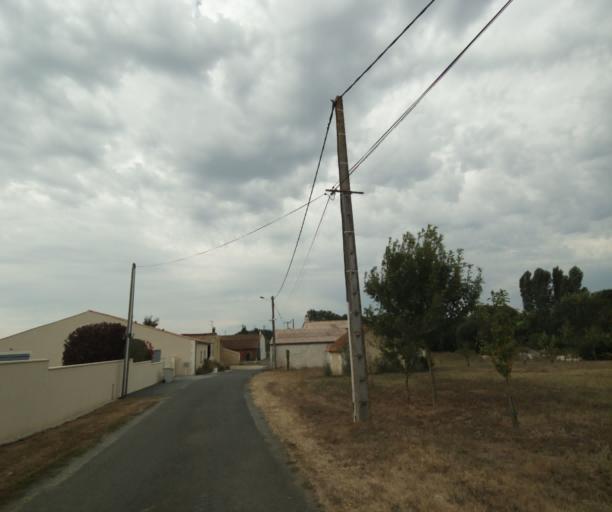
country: FR
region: Poitou-Charentes
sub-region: Departement de la Charente-Maritime
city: Tonnay-Charente
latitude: 45.9654
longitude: -0.8764
